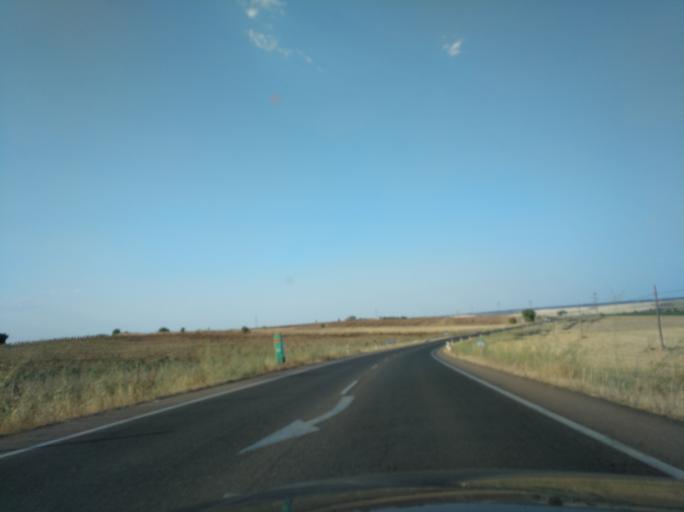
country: ES
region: Extremadura
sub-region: Provincia de Badajoz
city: Olivenza
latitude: 38.7224
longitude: -7.0814
